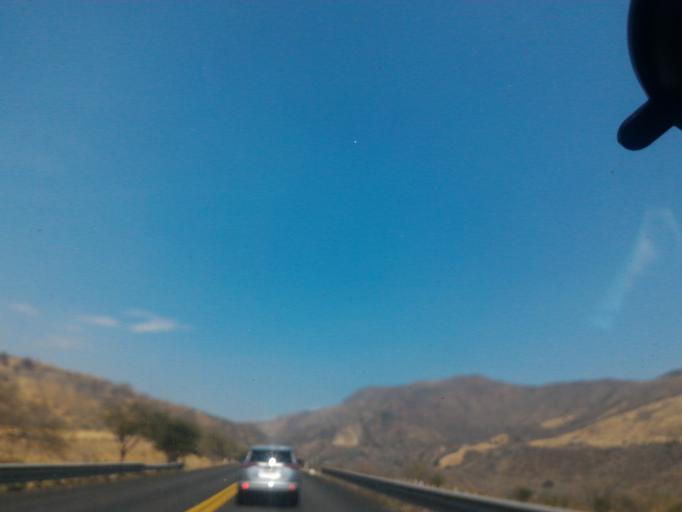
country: MX
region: Jalisco
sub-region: Tonila
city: San Marcos
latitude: 19.4853
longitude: -103.4521
